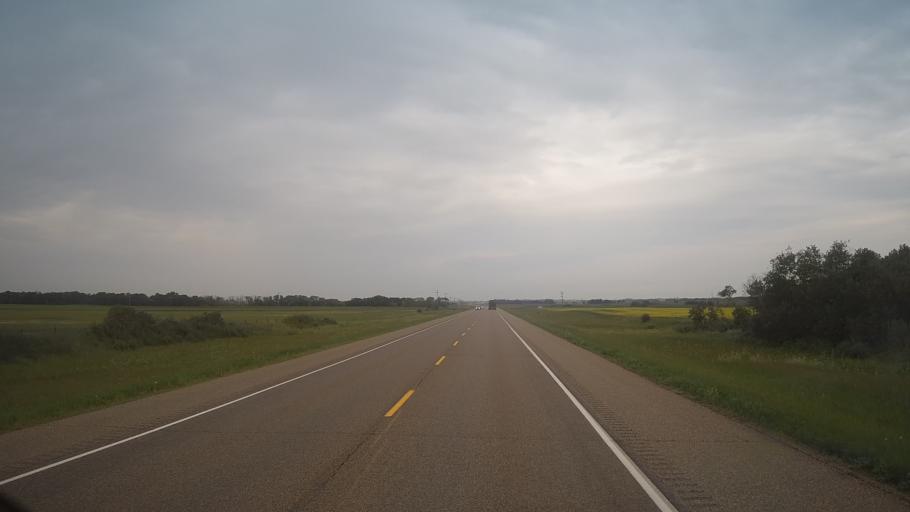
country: CA
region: Saskatchewan
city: Langham
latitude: 52.1294
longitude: -107.0912
